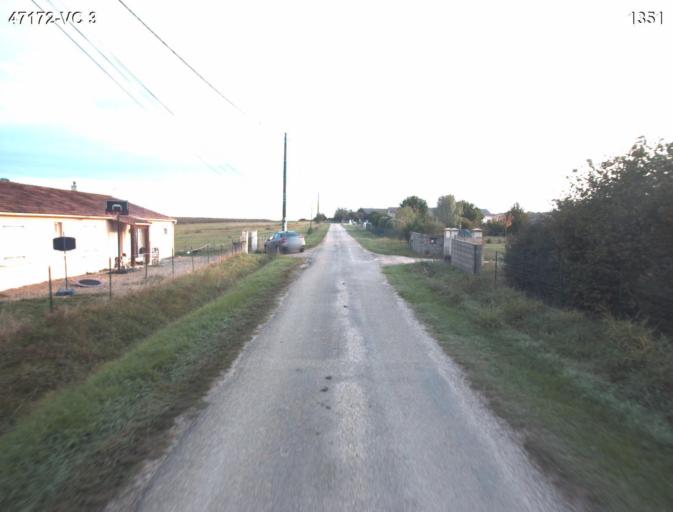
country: FR
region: Aquitaine
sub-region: Departement du Lot-et-Garonne
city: Sainte-Colombe-en-Bruilhois
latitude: 44.1584
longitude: 0.4952
